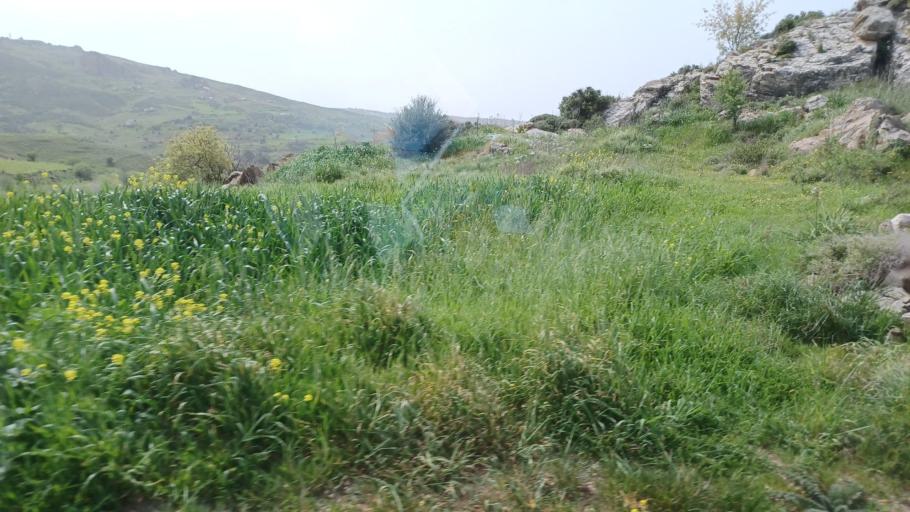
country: CY
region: Pafos
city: Polis
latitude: 34.9746
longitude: 32.3596
